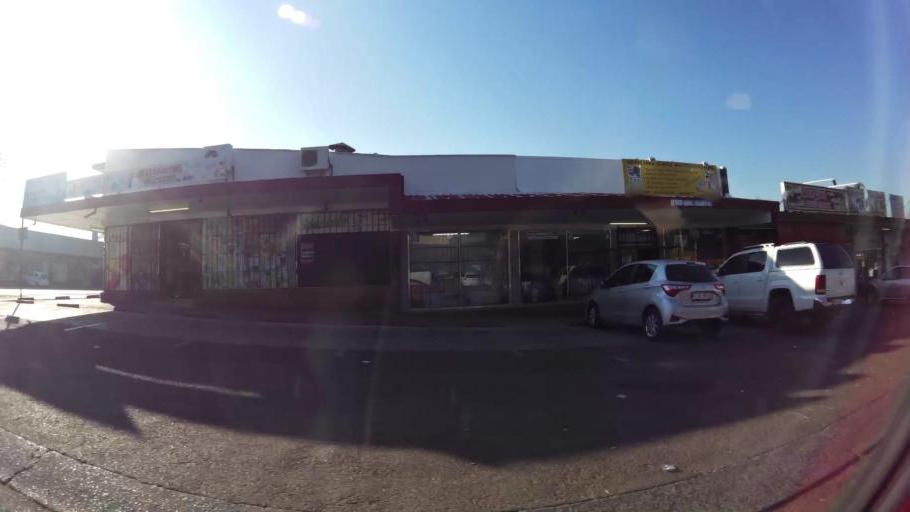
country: ZA
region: Gauteng
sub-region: City of Tshwane Metropolitan Municipality
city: Pretoria
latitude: -25.7009
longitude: 28.1587
